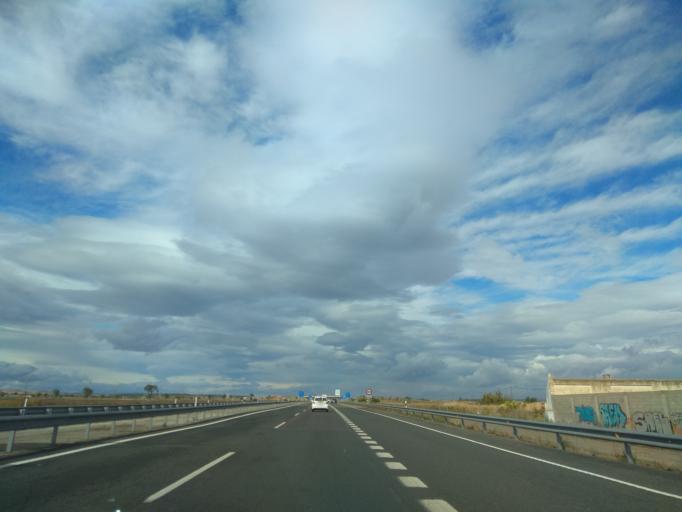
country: ES
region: Navarre
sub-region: Provincia de Navarra
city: Ribaforada
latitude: 41.9559
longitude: -1.4900
